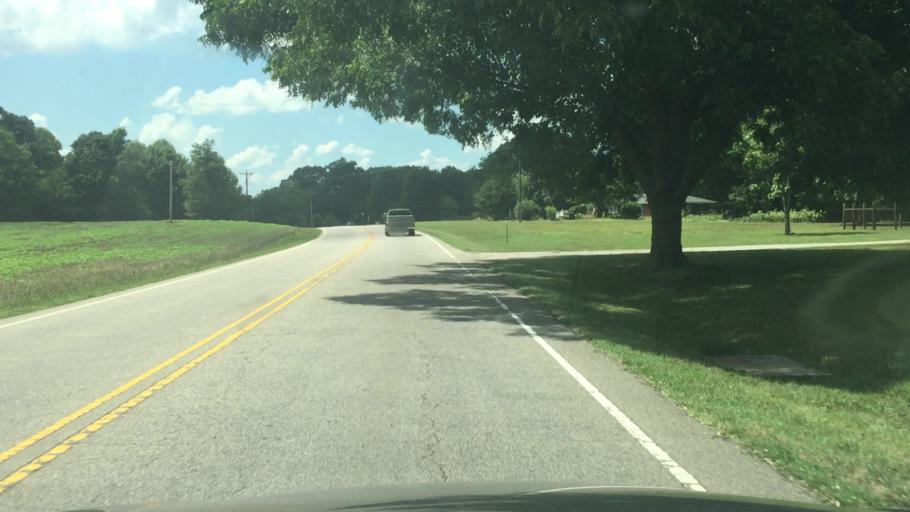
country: US
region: North Carolina
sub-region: Rowan County
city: Enochville
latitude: 35.5759
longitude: -80.6901
